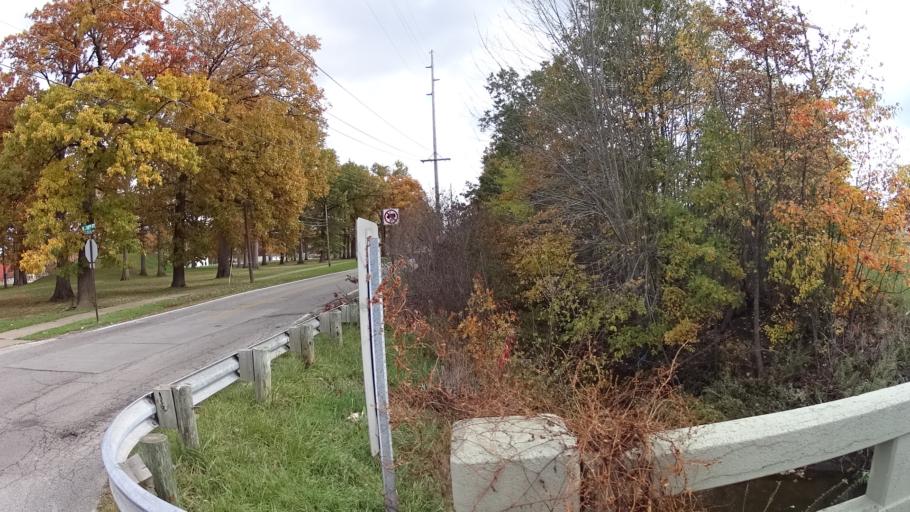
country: US
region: Ohio
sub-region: Lorain County
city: Sheffield
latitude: 41.4378
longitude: -82.1277
